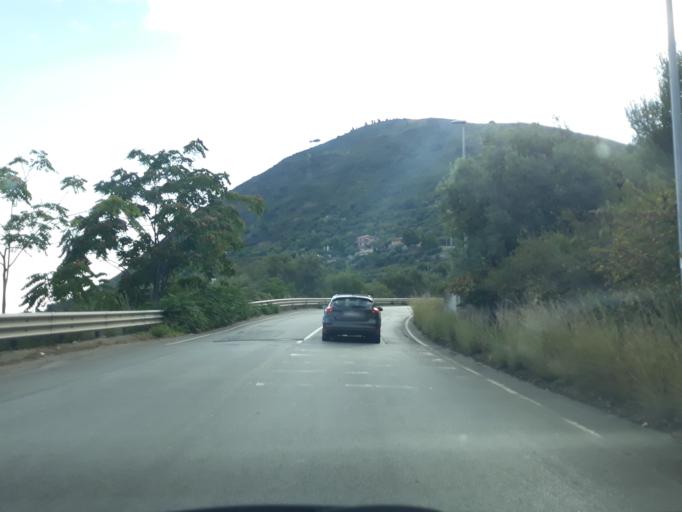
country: IT
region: Sicily
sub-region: Palermo
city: Cefalu
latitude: 38.0275
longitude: 14.0119
